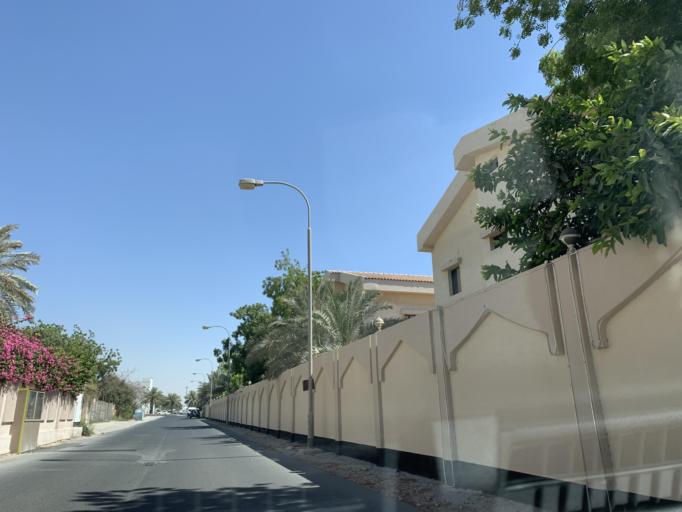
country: BH
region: Manama
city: Jidd Hafs
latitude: 26.2201
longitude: 50.4861
